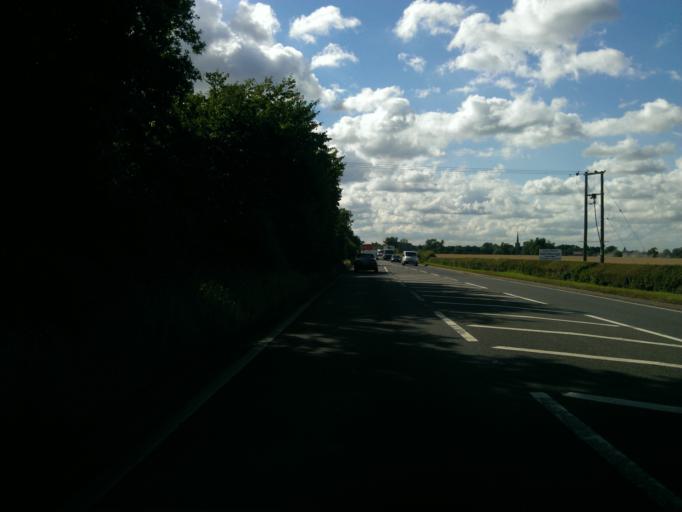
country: GB
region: England
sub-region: Warwickshire
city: Hartshill
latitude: 52.5652
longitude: -1.5056
